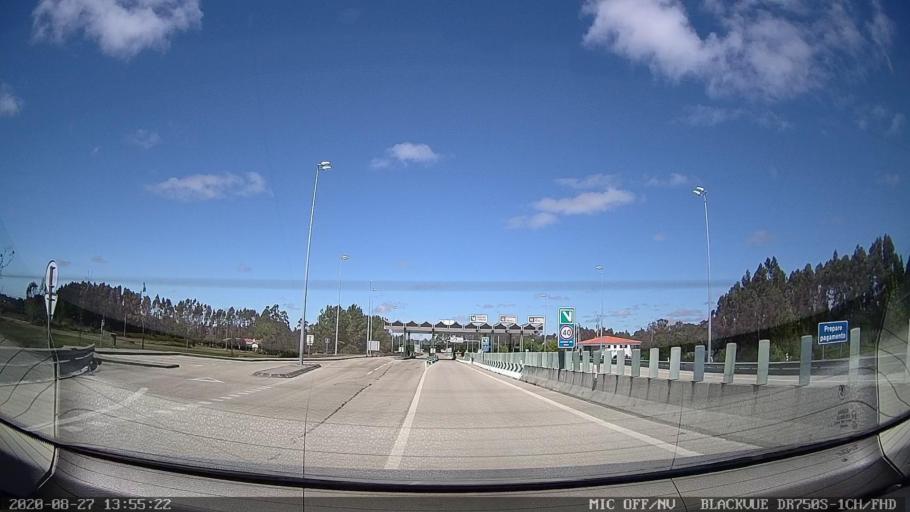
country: PT
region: Coimbra
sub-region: Montemor-O-Velho
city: Arazede
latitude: 40.3286
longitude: -8.7250
